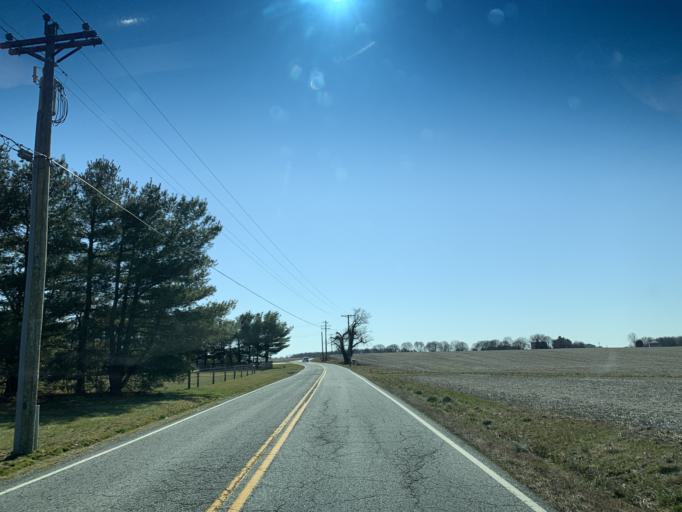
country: US
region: Maryland
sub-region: Cecil County
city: Charlestown
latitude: 39.4499
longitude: -75.9004
